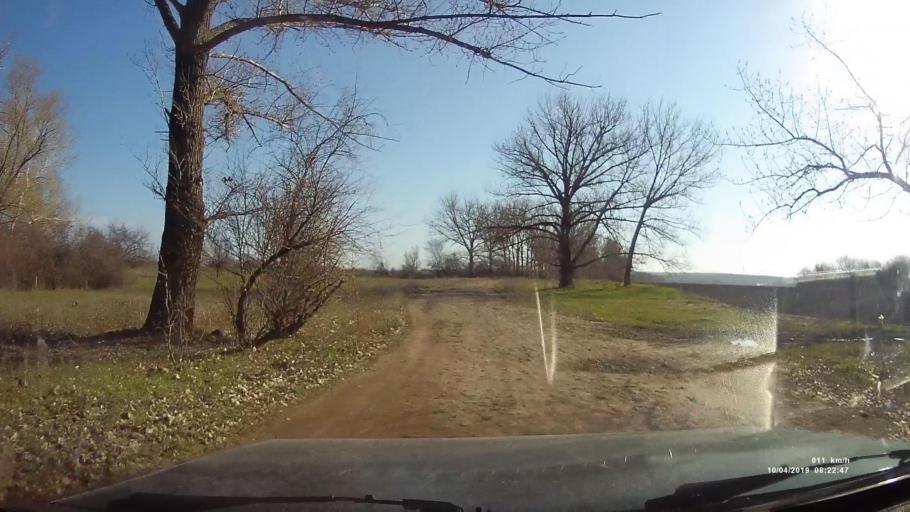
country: RU
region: Rostov
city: Kamensk-Shakhtinskiy
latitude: 48.3595
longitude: 40.2353
